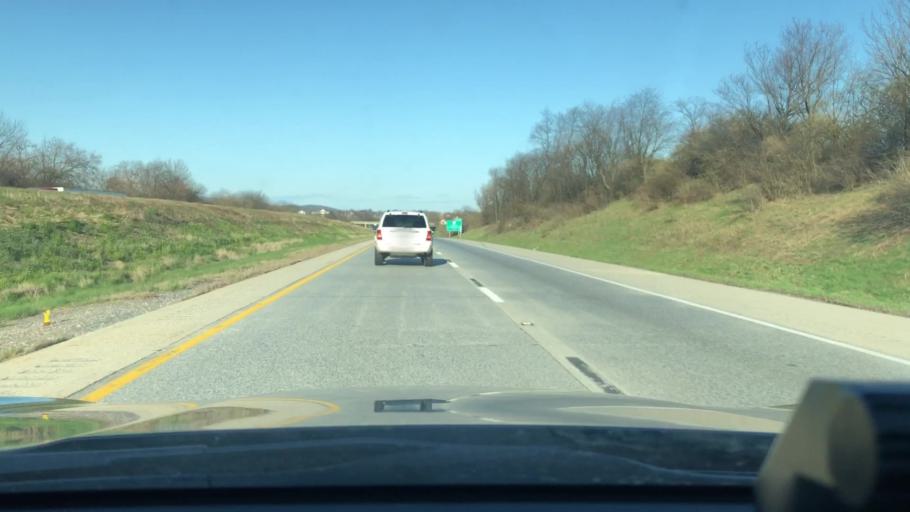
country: US
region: Pennsylvania
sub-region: Lebanon County
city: Fredericksburg
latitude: 40.4504
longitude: -76.4428
